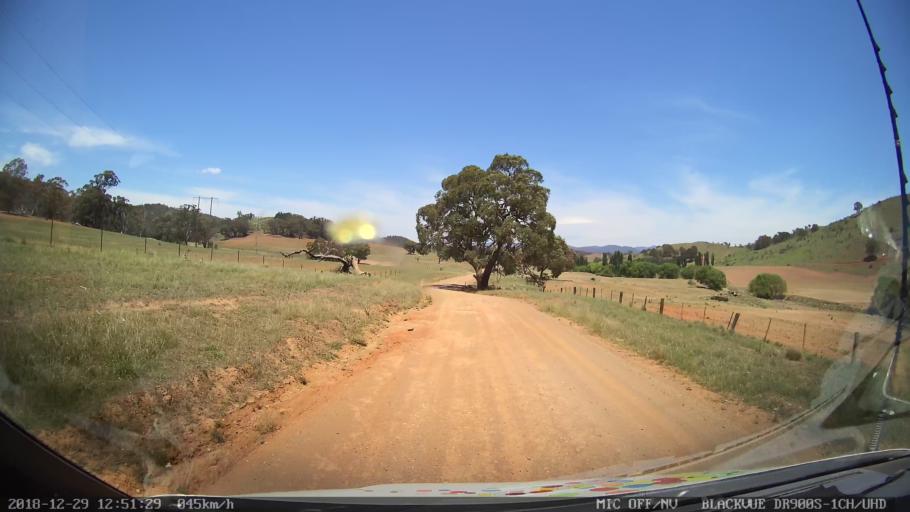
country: AU
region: Australian Capital Territory
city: Macarthur
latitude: -35.6751
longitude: 149.1986
